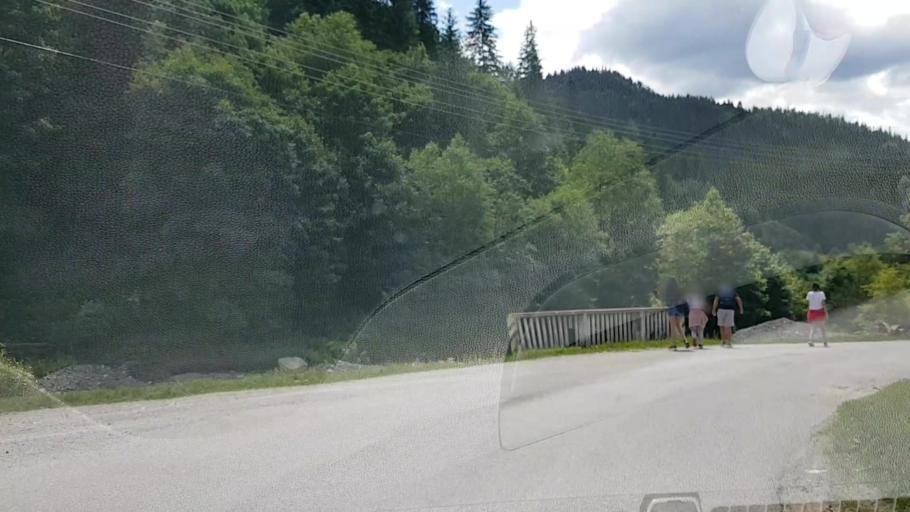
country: RO
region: Suceava
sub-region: Comuna Crucea
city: Crucea
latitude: 47.4156
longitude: 25.5853
